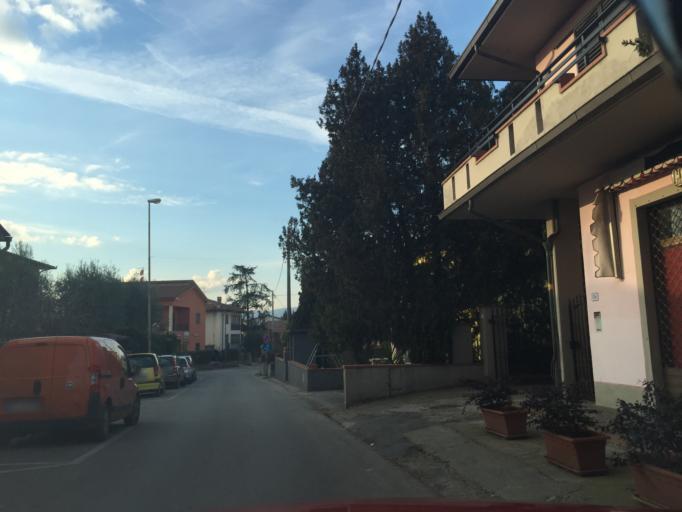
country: IT
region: Tuscany
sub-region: Provincia di Pistoia
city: Cintolese
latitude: 43.8571
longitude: 10.8350
